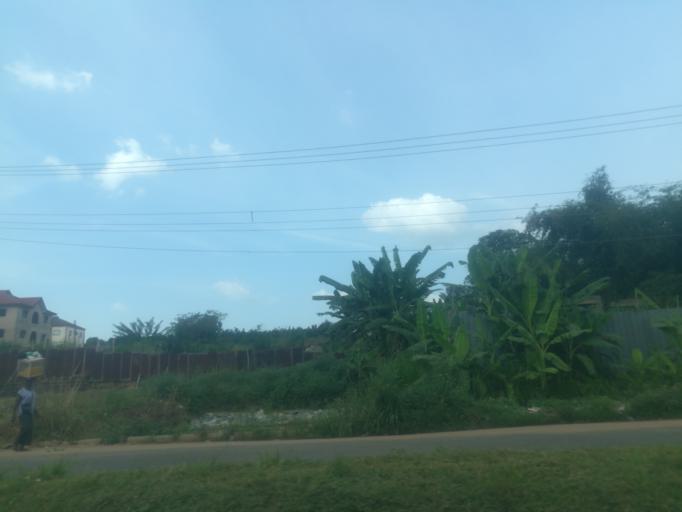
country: NG
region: Ogun
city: Abeokuta
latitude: 7.1362
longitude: 3.3254
